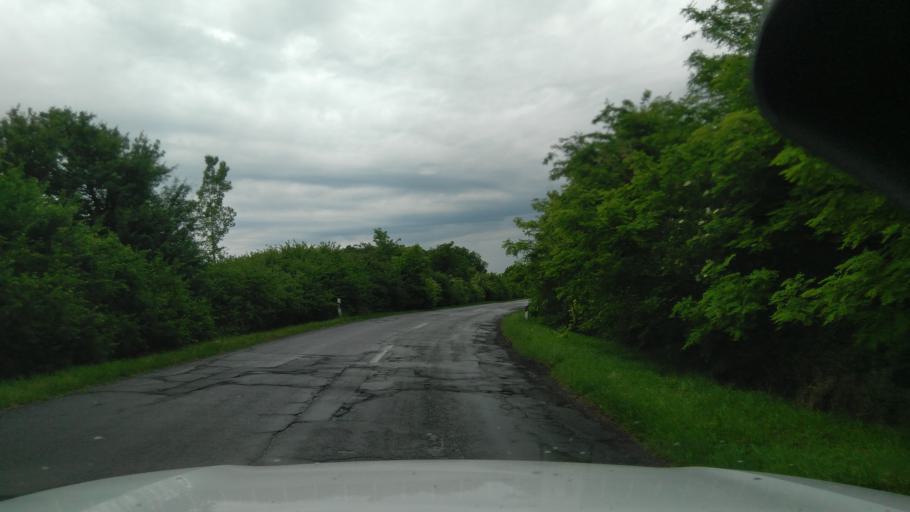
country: HU
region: Bekes
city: Bekescsaba
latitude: 46.6843
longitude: 21.1663
